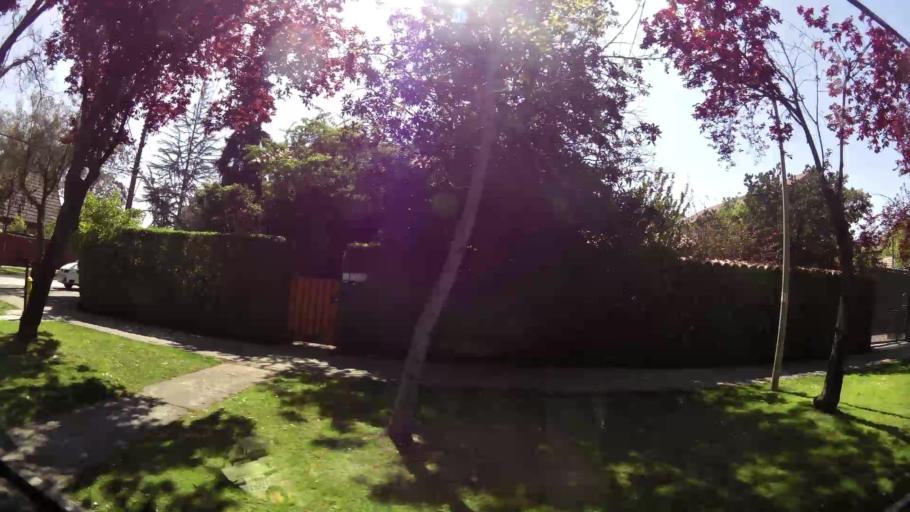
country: CL
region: Santiago Metropolitan
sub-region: Provincia de Santiago
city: Villa Presidente Frei, Nunoa, Santiago, Chile
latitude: -33.4243
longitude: -70.5574
